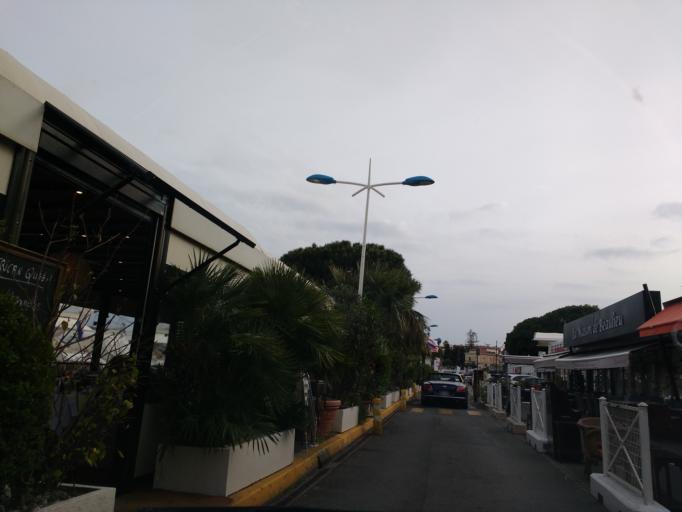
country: FR
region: Provence-Alpes-Cote d'Azur
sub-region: Departement des Alpes-Maritimes
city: Beaulieu-sur-Mer
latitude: 43.7101
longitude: 7.3357
